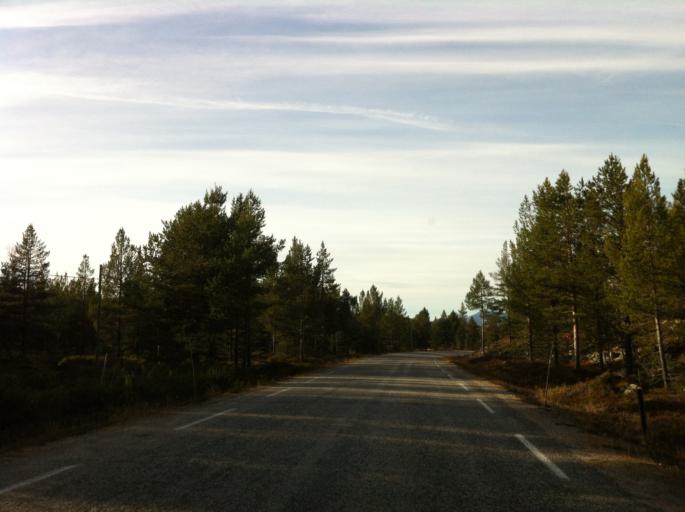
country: NO
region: Hedmark
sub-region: Engerdal
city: Engerdal
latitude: 62.1202
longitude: 12.0100
